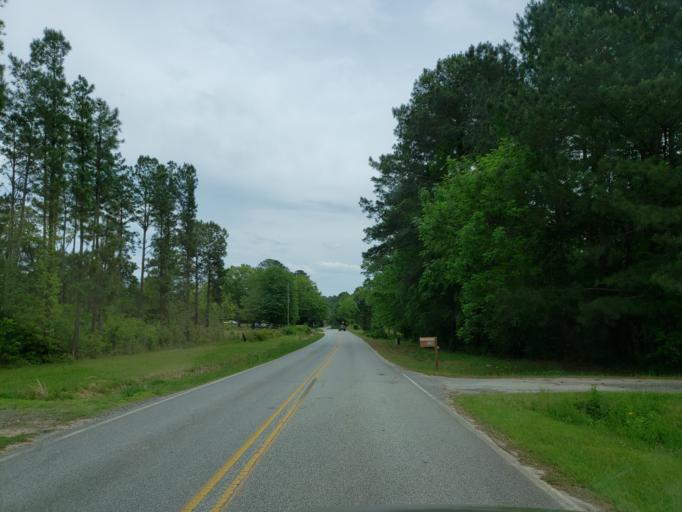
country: US
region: Georgia
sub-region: Bibb County
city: West Point
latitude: 32.8213
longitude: -83.8668
